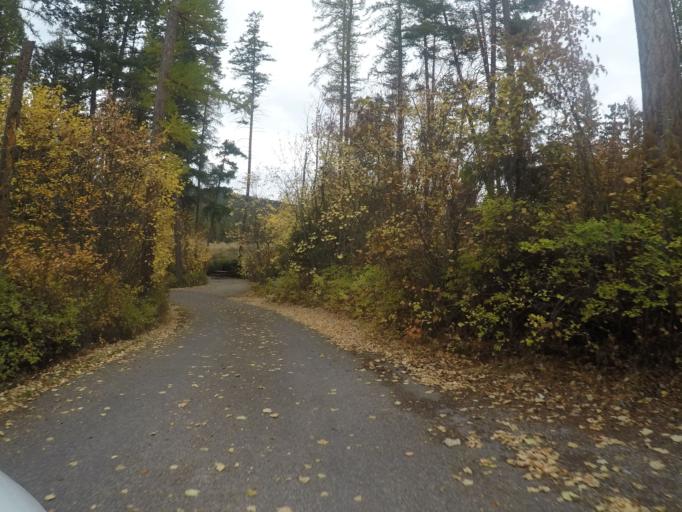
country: US
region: Montana
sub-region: Flathead County
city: Bigfork
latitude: 48.0524
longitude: -114.0817
